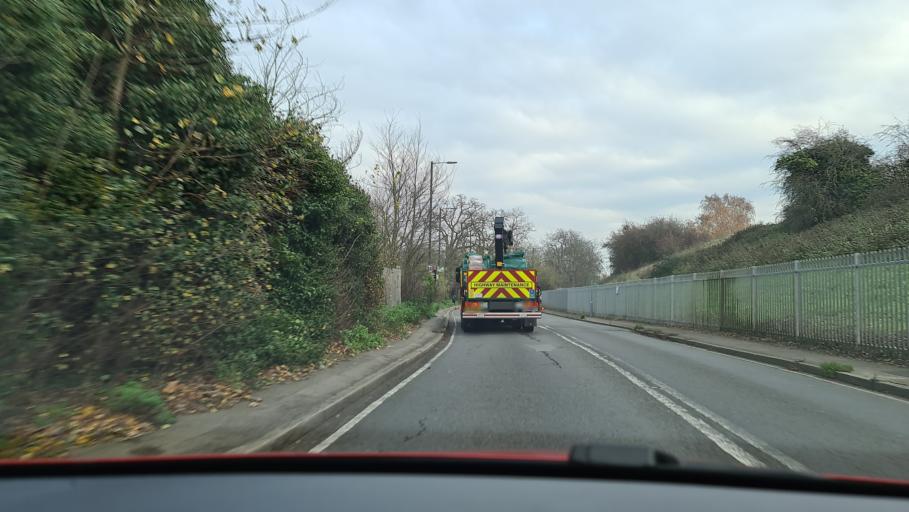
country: GB
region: England
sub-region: Surrey
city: West Molesey
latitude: 51.4144
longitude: -0.3869
